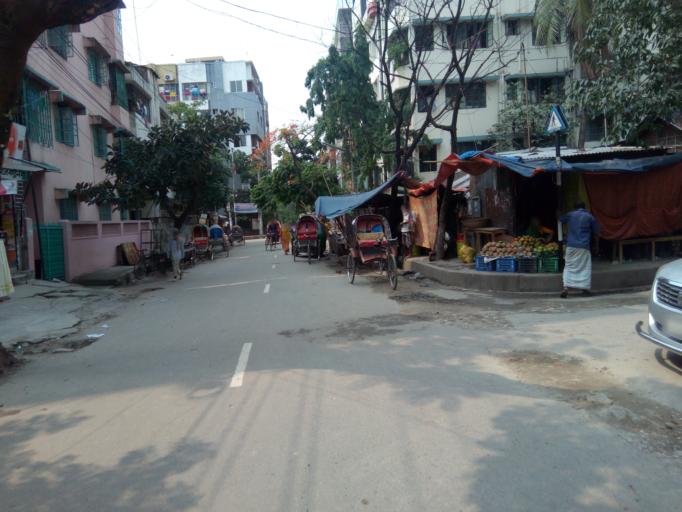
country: BD
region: Dhaka
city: Paltan
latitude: 23.7532
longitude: 90.4202
